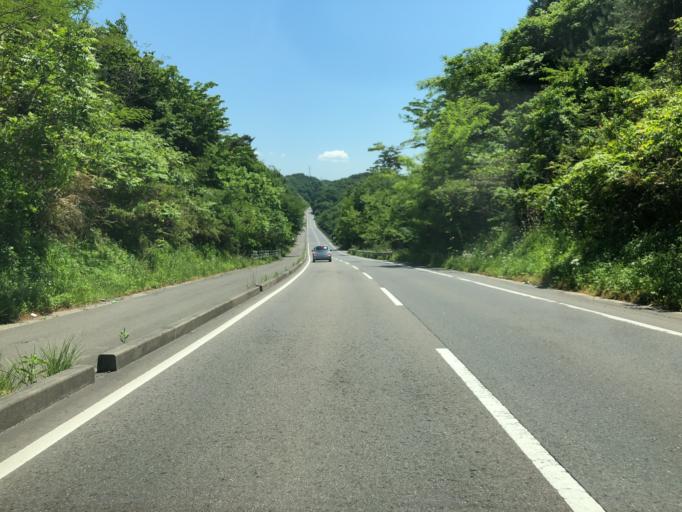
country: JP
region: Fukushima
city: Motomiya
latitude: 37.5363
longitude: 140.4124
